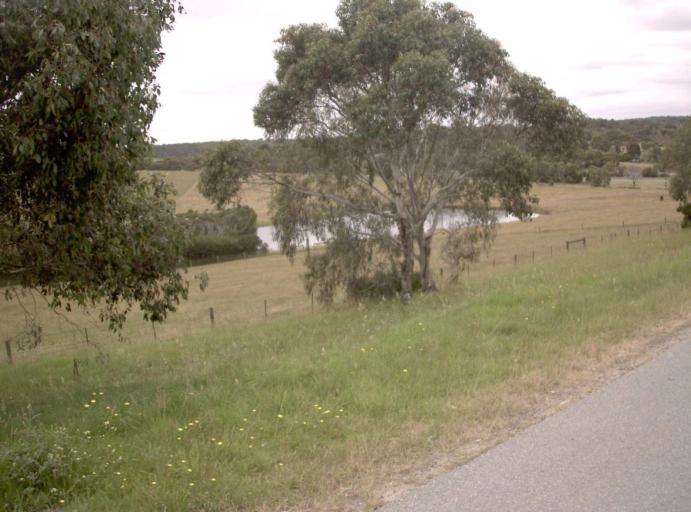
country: AU
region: Victoria
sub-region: Mornington Peninsula
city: Mount Martha
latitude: -38.2968
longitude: 145.0314
